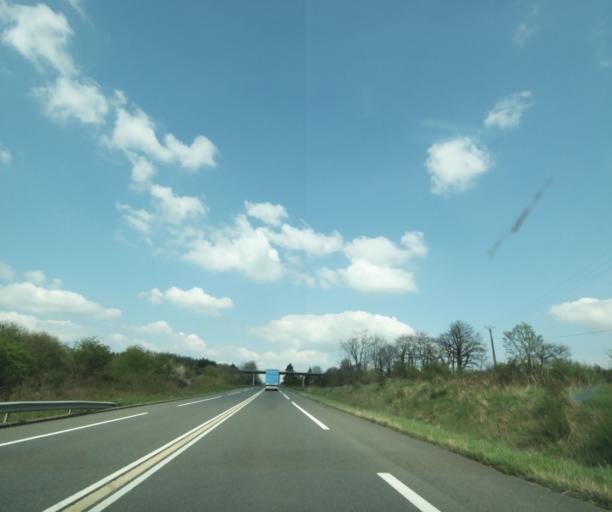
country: FR
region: Auvergne
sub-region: Departement de l'Allier
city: Montmarault
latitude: 46.3420
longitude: 2.9863
